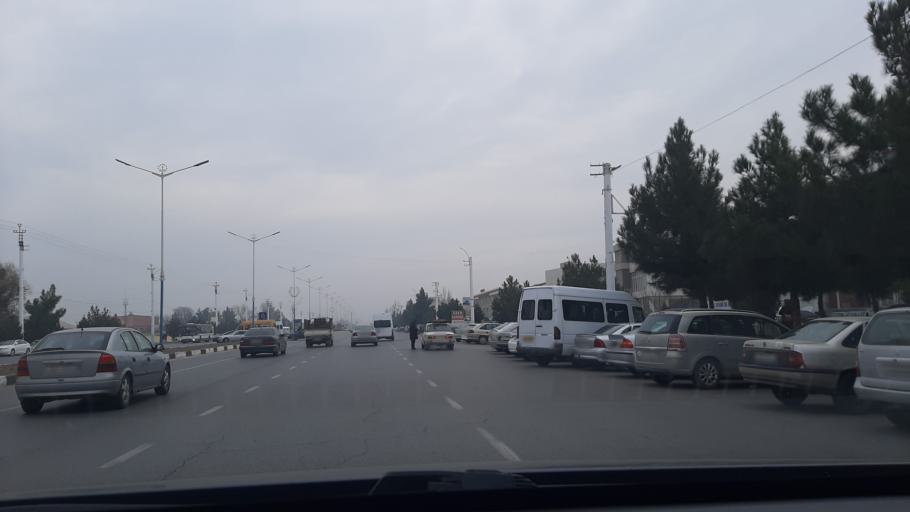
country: TJ
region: Viloyati Sughd
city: Chkalov
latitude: 40.2429
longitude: 69.7035
